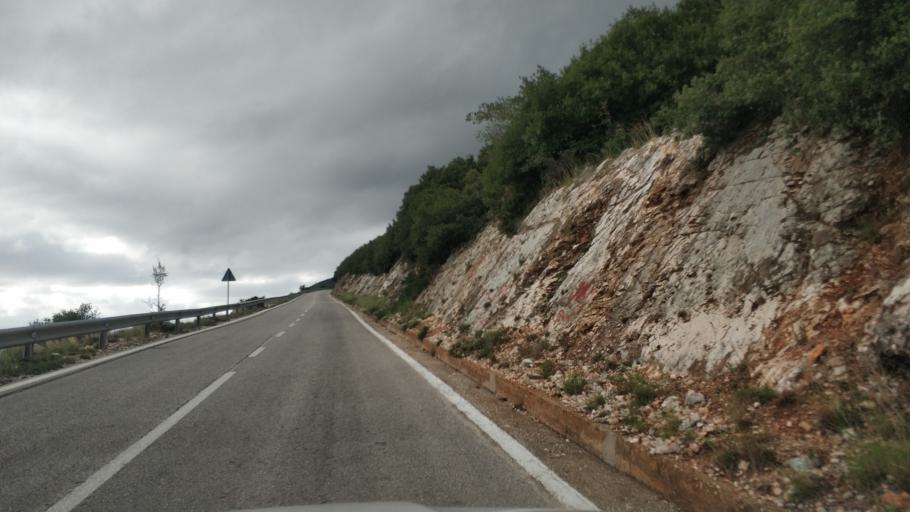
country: AL
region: Vlore
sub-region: Rrethi i Vlores
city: Vranisht
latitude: 40.1778
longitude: 19.6026
